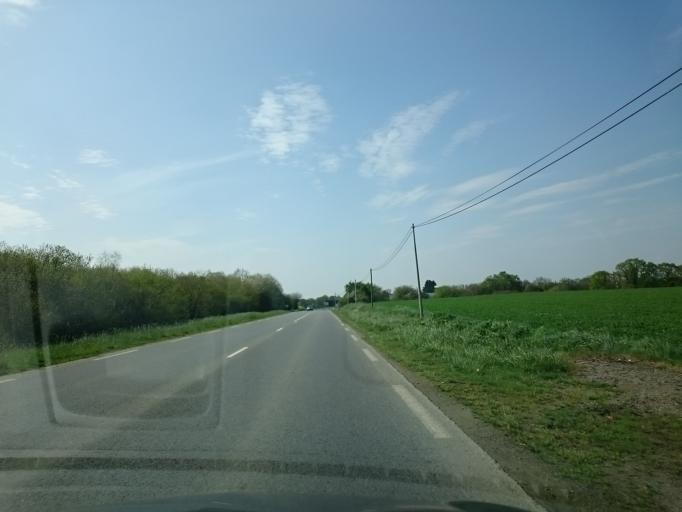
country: FR
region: Brittany
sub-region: Departement d'Ille-et-Vilaine
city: Chantepie
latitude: 48.0778
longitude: -1.5929
